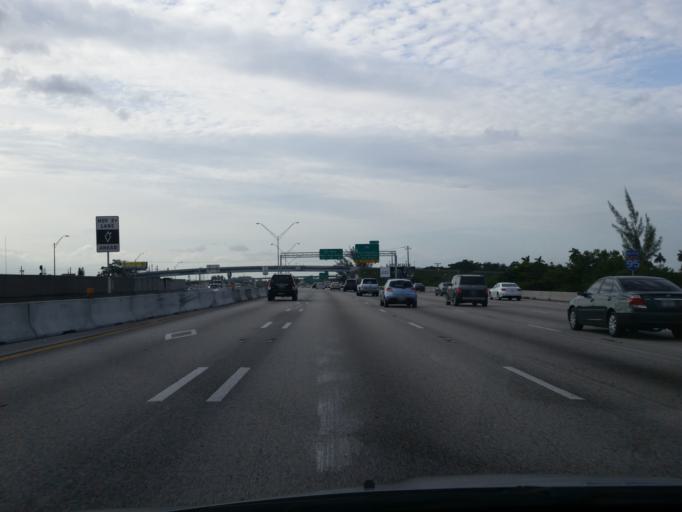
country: US
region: Florida
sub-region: Broward County
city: Dania Beach
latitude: 26.0670
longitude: -80.1651
